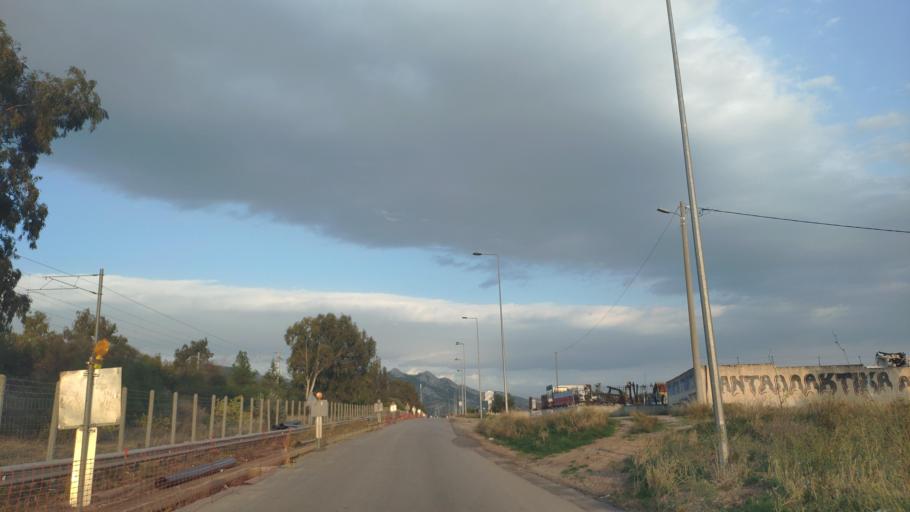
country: GR
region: Attica
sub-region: Nomarchia Dytikis Attikis
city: Nea Peramos
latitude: 38.0106
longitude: 23.4093
